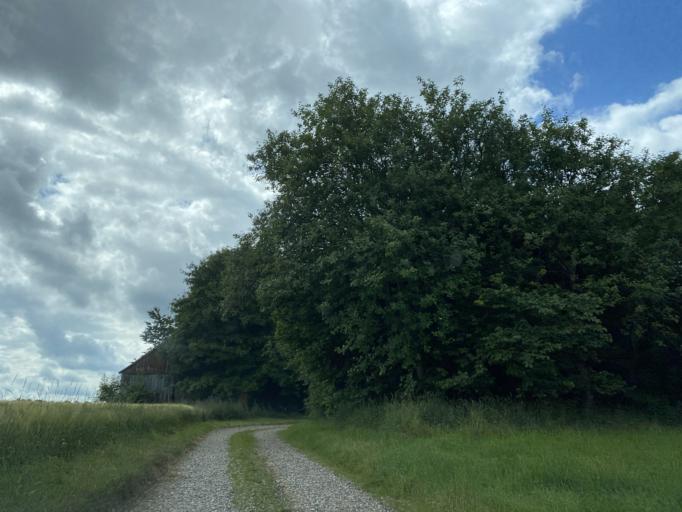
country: DK
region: Central Jutland
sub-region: Silkeborg Kommune
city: Silkeborg
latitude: 56.2113
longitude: 9.5749
